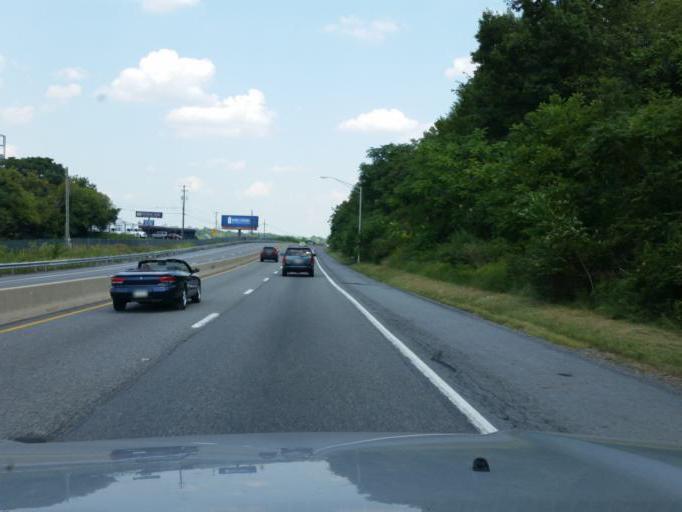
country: US
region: Pennsylvania
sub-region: Dauphin County
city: Lawnton
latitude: 40.2554
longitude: -76.7957
